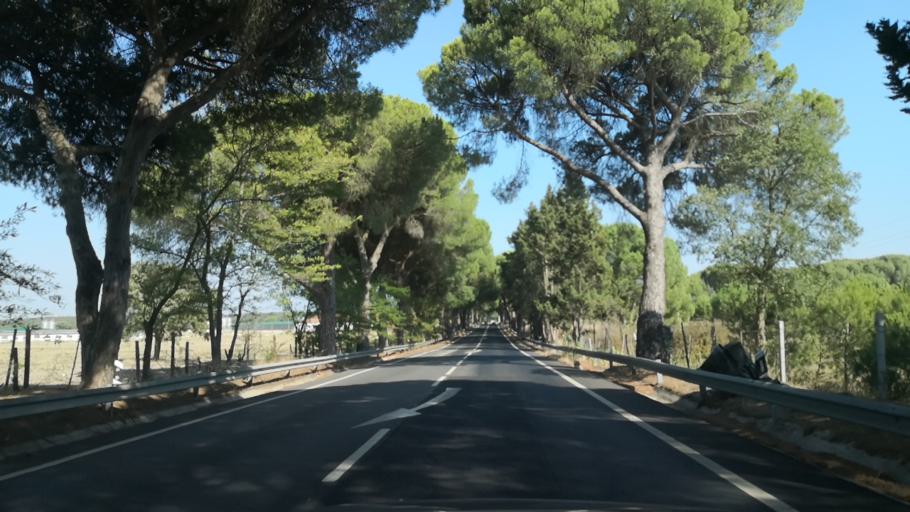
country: PT
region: Evora
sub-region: Vendas Novas
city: Vendas Novas
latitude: 38.7193
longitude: -8.6263
